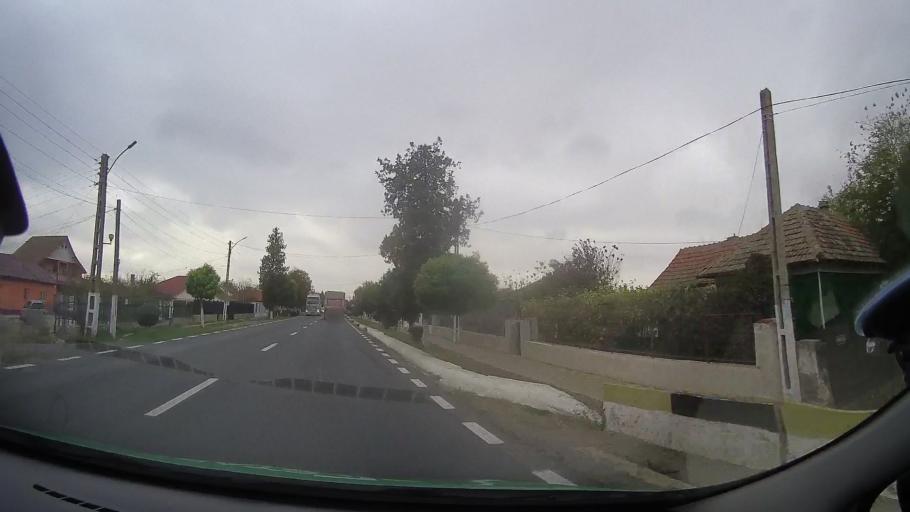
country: RO
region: Constanta
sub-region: Comuna Castelu
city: Castelu
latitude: 44.2575
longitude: 28.3413
